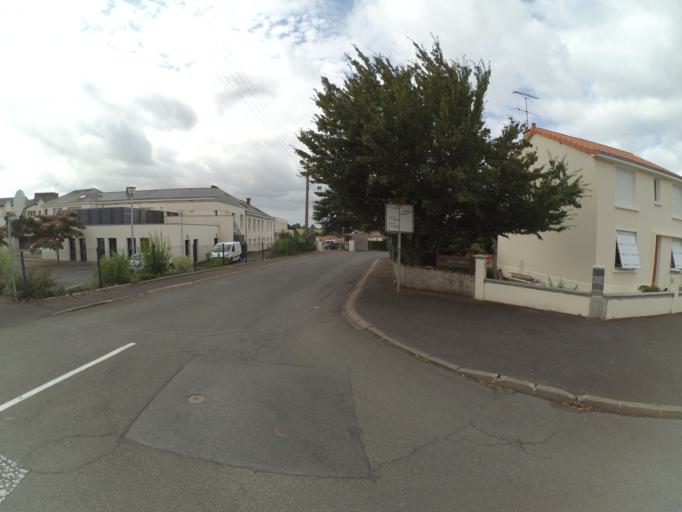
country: FR
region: Pays de la Loire
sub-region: Departement de Maine-et-Loire
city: Jallais
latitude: 47.1972
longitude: -0.8745
